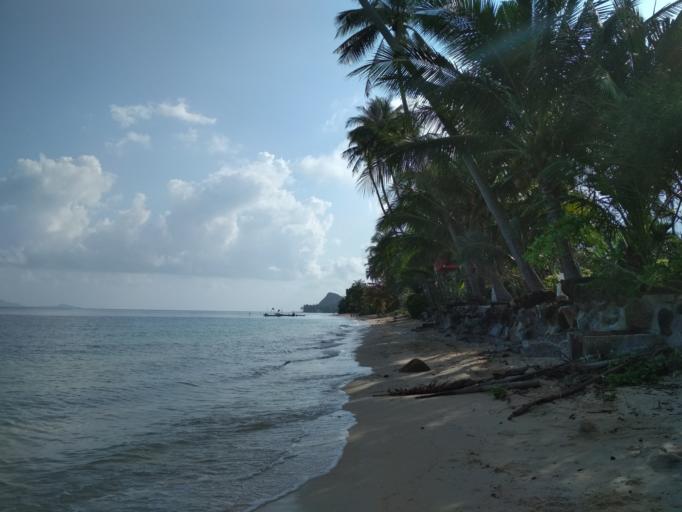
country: TH
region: Surat Thani
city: Ko Samui
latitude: 9.5791
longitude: 99.9532
